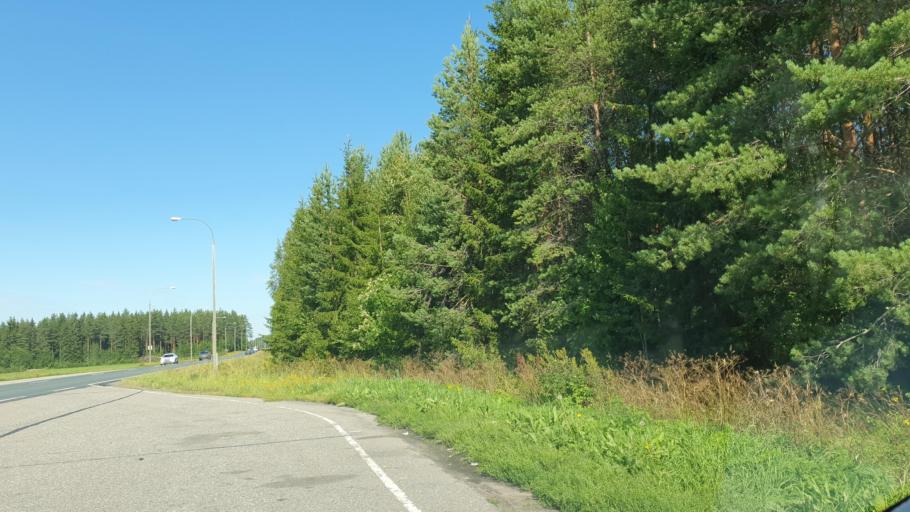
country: FI
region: Northern Savo
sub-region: Ylae-Savo
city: Lapinlahti
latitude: 63.3379
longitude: 27.4264
